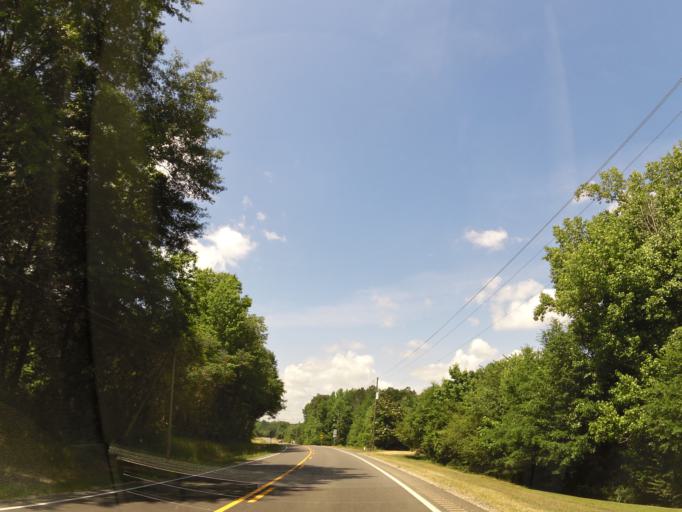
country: US
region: Alabama
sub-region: Marion County
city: Guin
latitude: 33.9308
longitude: -88.0220
